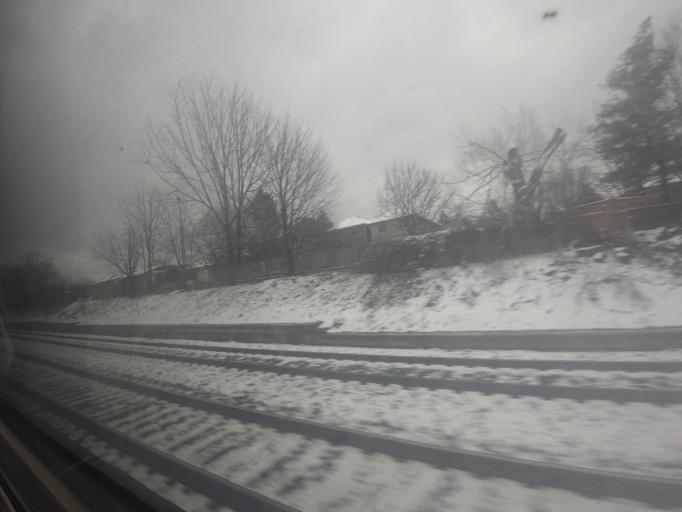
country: CA
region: Ontario
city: Scarborough
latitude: 43.7063
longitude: -79.2620
